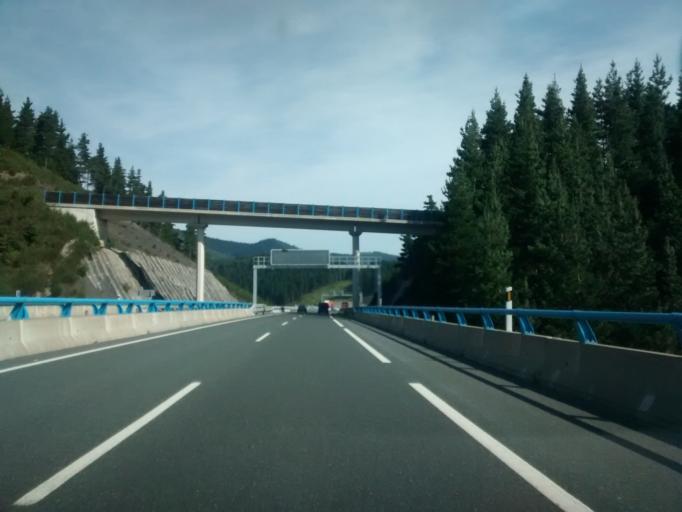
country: ES
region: Basque Country
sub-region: Provincia de Guipuzcoa
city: Leintz-Gatzaga
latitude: 42.9999
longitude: -2.5731
